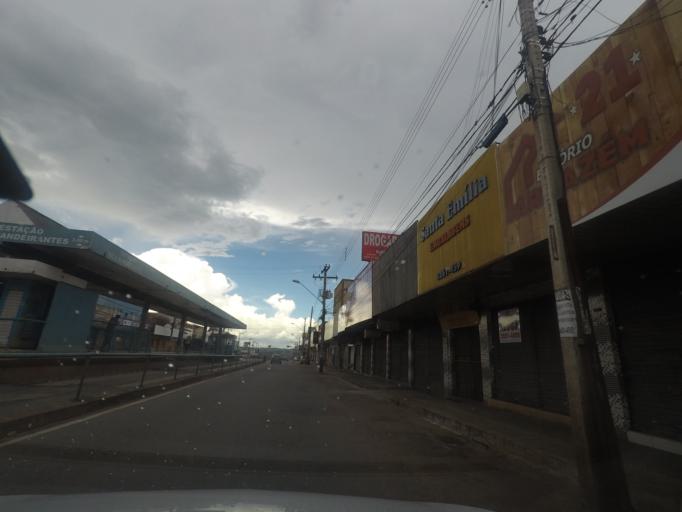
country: BR
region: Goias
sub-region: Goiania
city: Goiania
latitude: -16.6710
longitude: -49.2315
